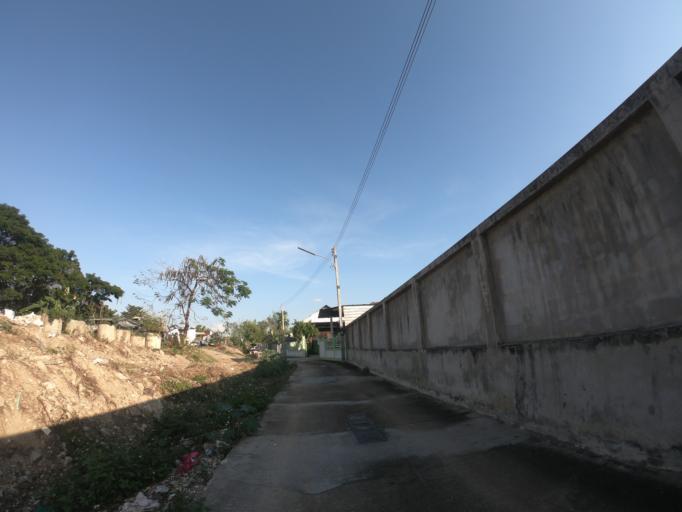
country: TH
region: Chiang Mai
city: Chiang Mai
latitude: 18.7434
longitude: 98.9819
